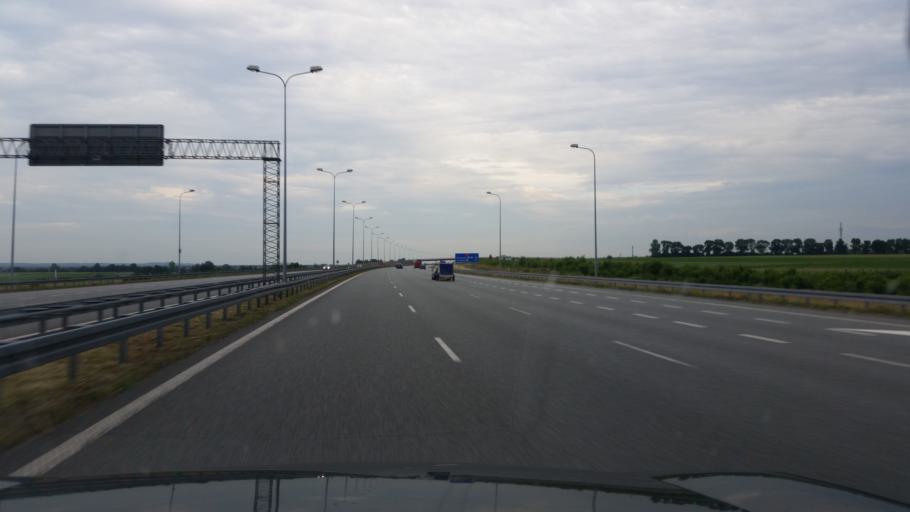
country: PL
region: Silesian Voivodeship
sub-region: Powiat gliwicki
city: Gieraltowice
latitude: 50.2493
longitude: 18.7149
